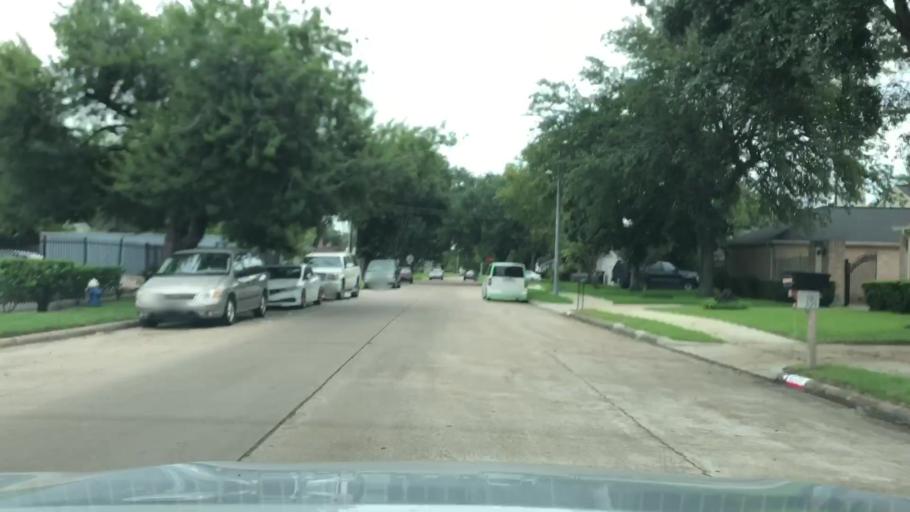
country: US
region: Texas
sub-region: Fort Bend County
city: Meadows Place
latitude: 29.7007
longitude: -95.5510
